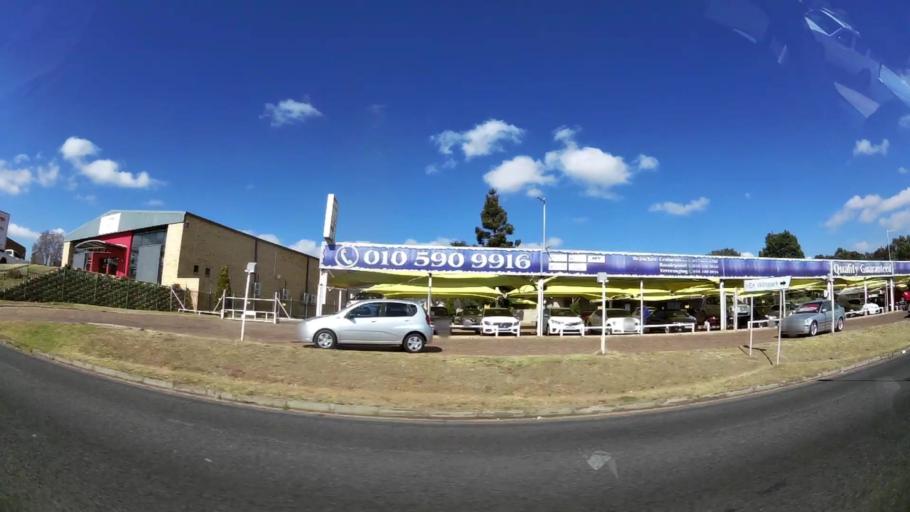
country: ZA
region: Gauteng
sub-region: City of Johannesburg Metropolitan Municipality
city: Roodepoort
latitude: -26.1269
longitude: 27.8410
